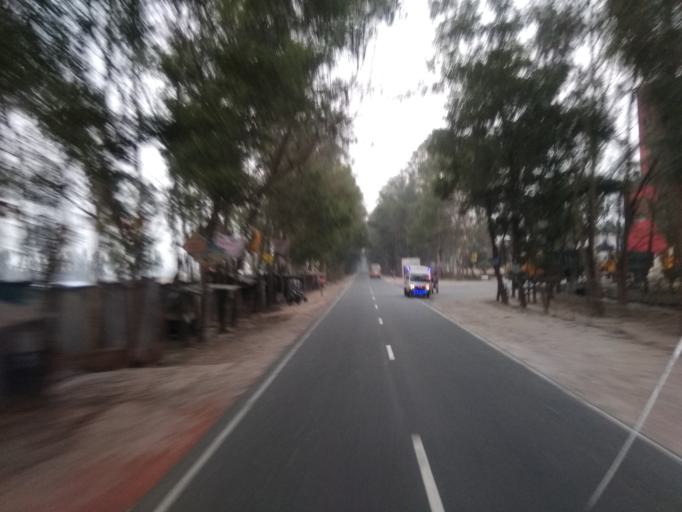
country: BD
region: Rajshahi
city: Bogra
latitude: 24.6655
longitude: 89.2724
